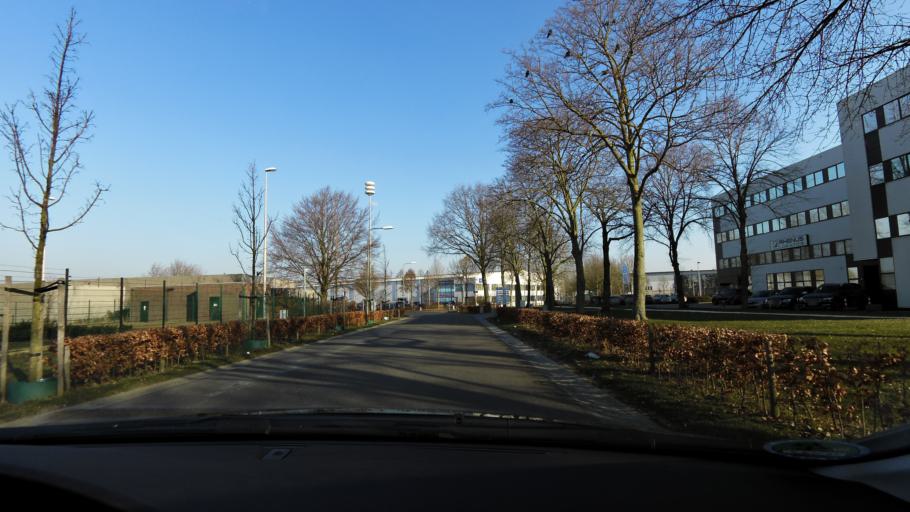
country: NL
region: Limburg
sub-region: Gemeente Beek
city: Beek
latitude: 50.9200
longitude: 5.7855
